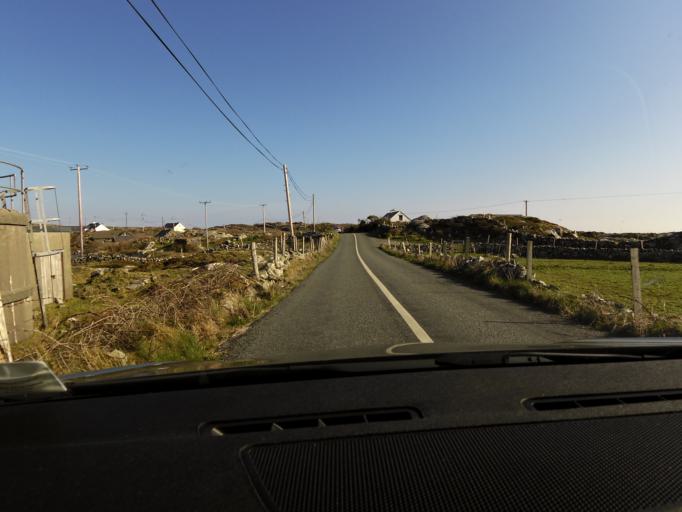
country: IE
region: Connaught
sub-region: County Galway
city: Clifden
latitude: 53.3977
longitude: -10.0284
